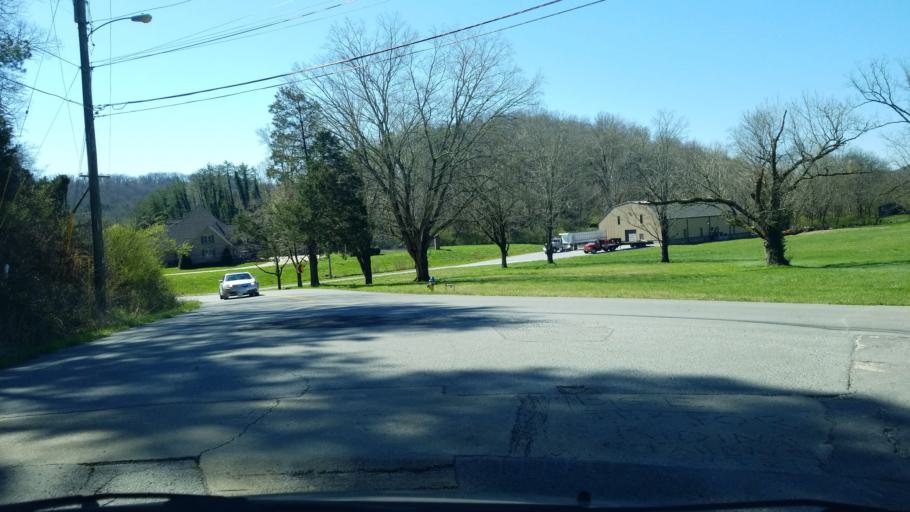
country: US
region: Tennessee
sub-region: Hamilton County
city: Falling Water
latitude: 35.1738
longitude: -85.2591
